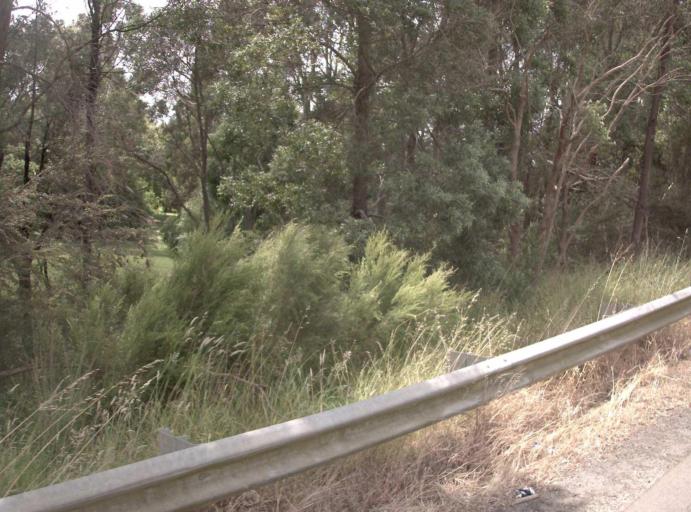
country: AU
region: Victoria
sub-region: Baw Baw
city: Warragul
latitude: -38.1709
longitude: 145.9697
